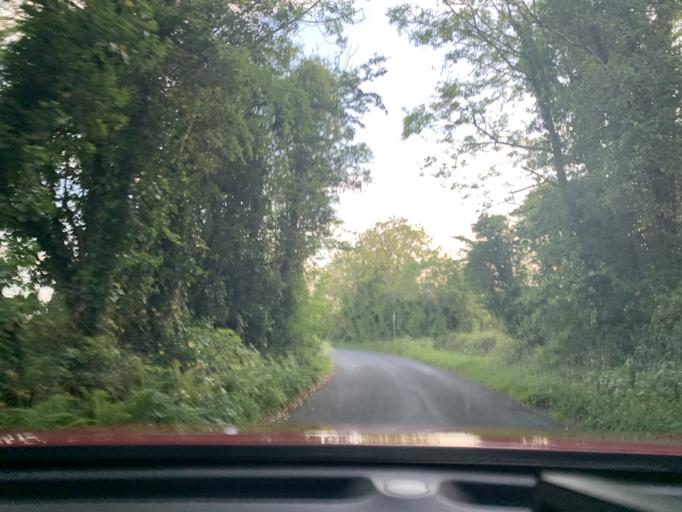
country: IE
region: Connaught
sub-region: Sligo
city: Sligo
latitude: 54.2908
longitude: -8.4585
